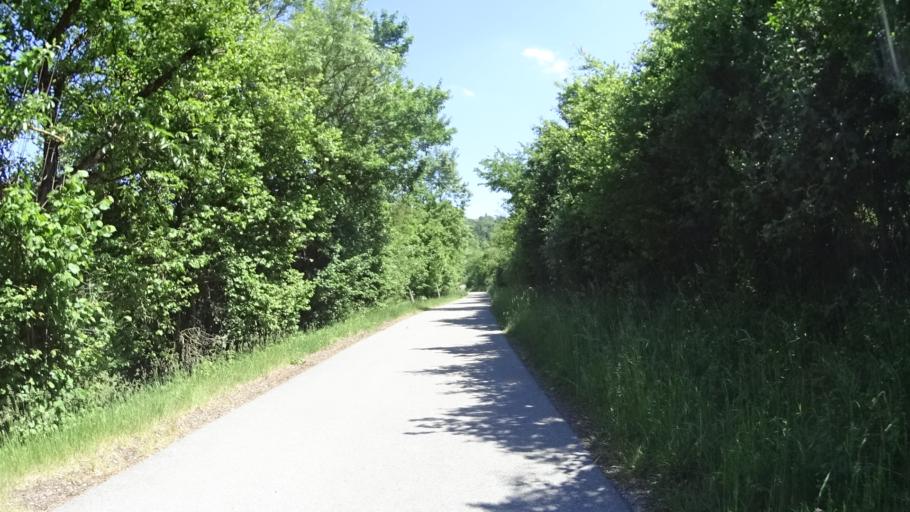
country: DE
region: Bavaria
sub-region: Regierungsbezirk Mittelfranken
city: Rothenburg ob der Tauber
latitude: 49.3973
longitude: 10.1624
